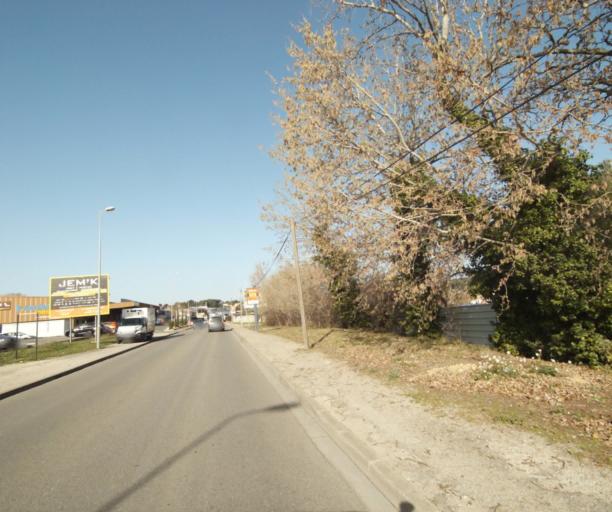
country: FR
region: Provence-Alpes-Cote d'Azur
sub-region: Departement des Bouches-du-Rhone
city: Septemes-les-Vallons
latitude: 43.4139
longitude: 5.3552
